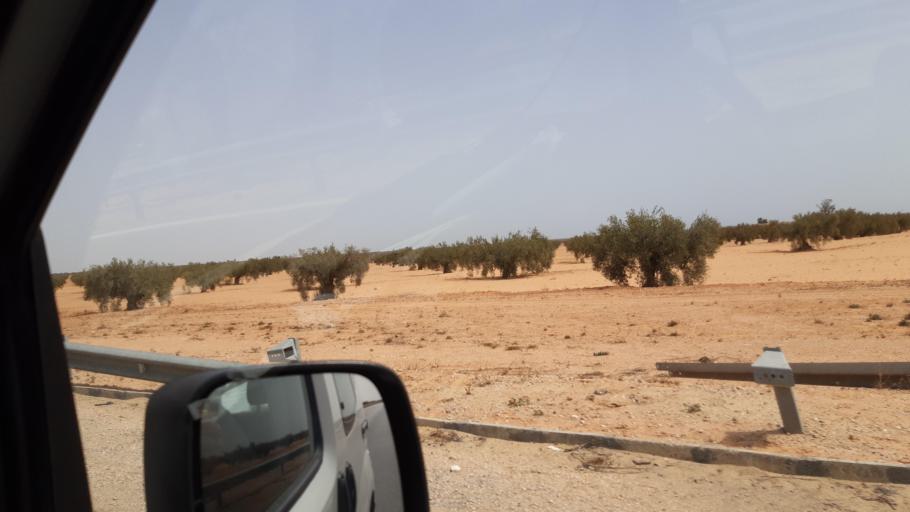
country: TN
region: Safaqis
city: Bi'r `Ali Bin Khalifah
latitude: 34.5574
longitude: 10.3340
